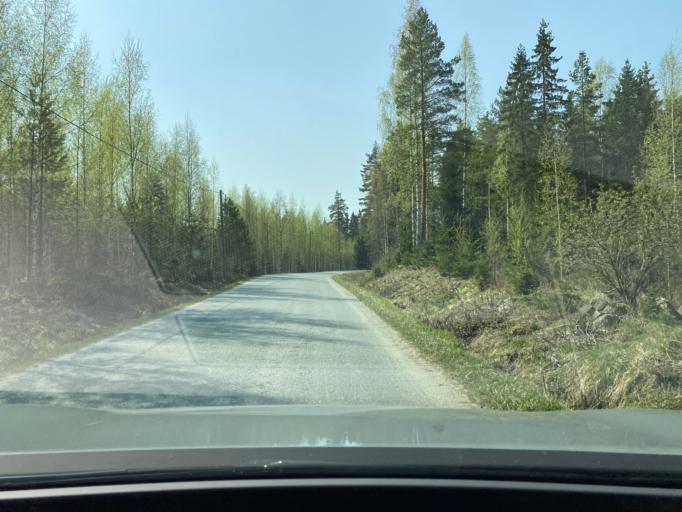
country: FI
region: Satakunta
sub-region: Pori
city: Huittinen
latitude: 61.1259
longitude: 22.8110
